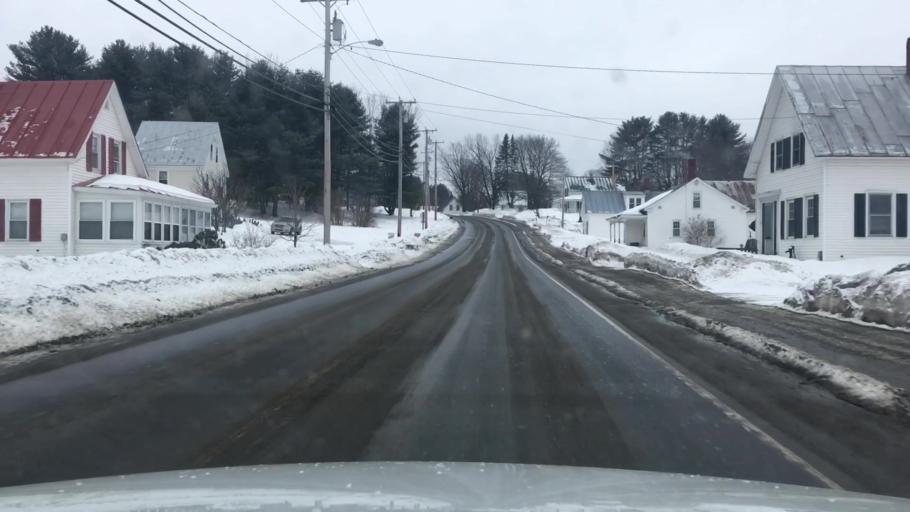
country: US
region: Maine
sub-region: Somerset County
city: Norridgewock
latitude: 44.7113
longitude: -69.7905
